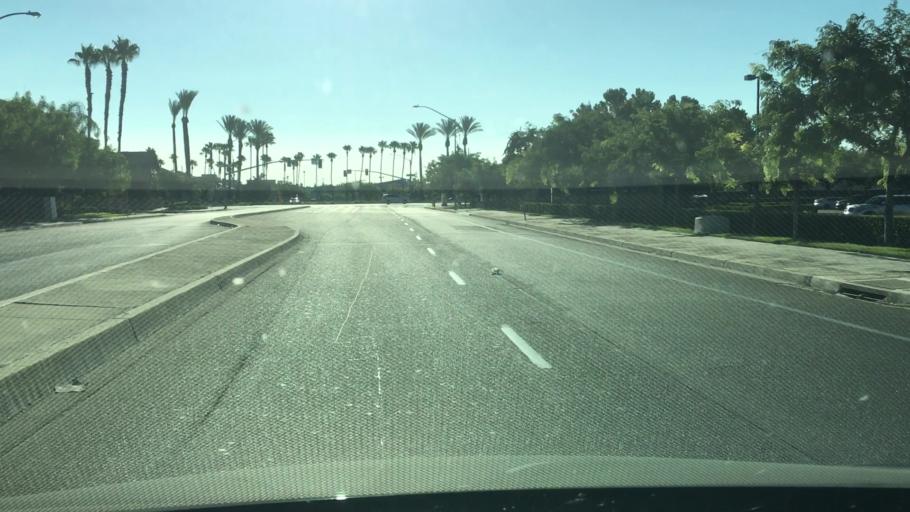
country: US
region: California
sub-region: Fresno County
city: Clovis
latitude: 36.8461
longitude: -119.7925
